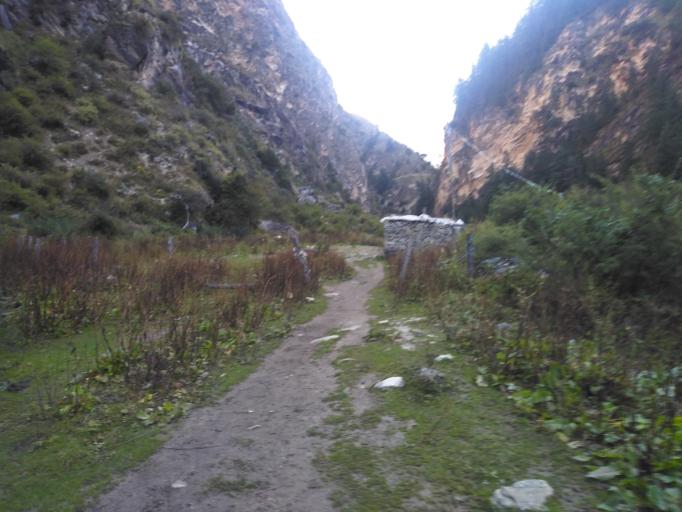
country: NP
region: Western Region
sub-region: Dhawalagiri Zone
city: Jomsom
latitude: 28.9299
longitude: 83.0431
